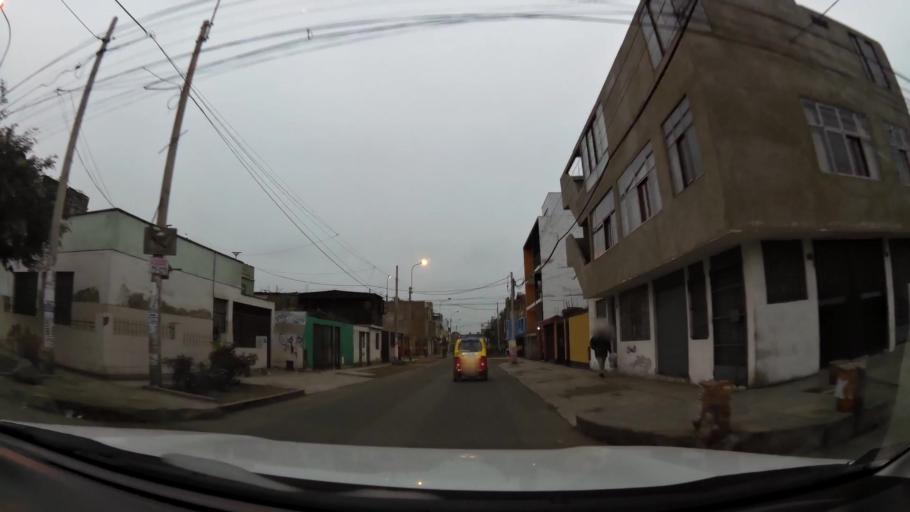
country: PE
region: Lima
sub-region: Lima
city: Surco
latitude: -12.1675
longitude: -76.9709
